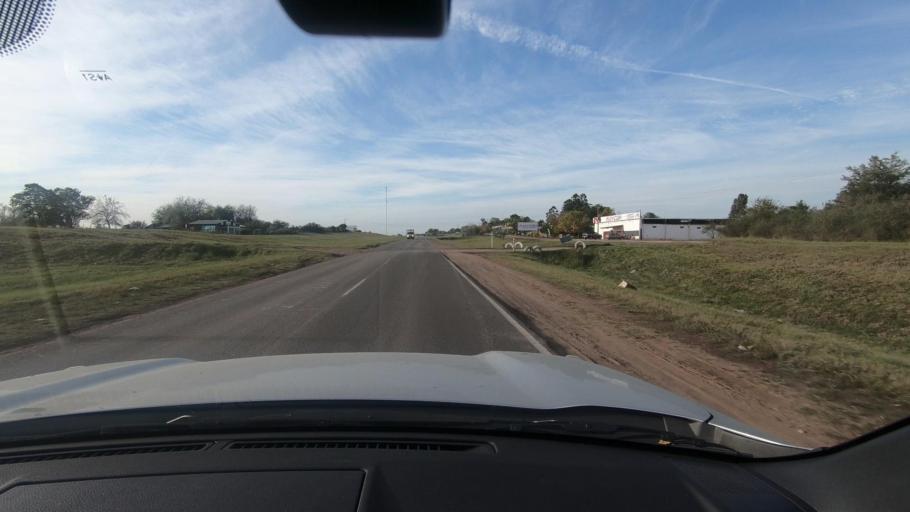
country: AR
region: Entre Rios
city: Colon
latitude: -32.2499
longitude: -58.2032
